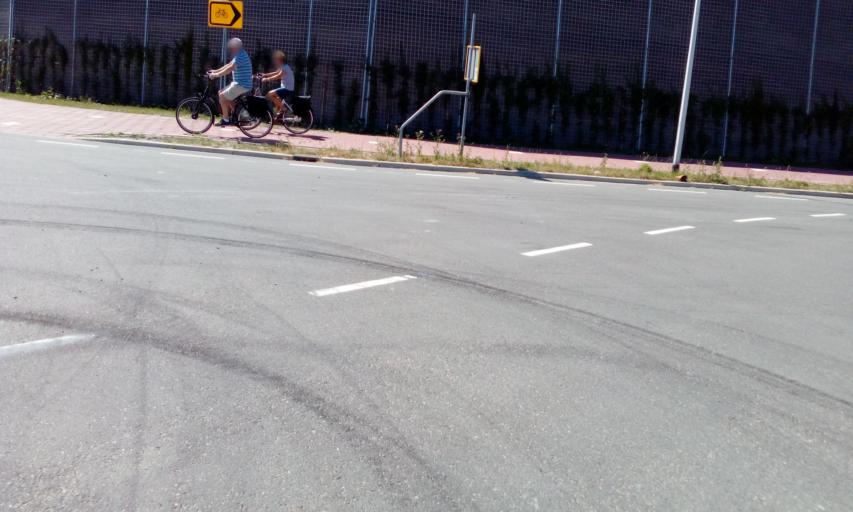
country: NL
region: South Holland
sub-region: Gemeente Westland
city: Honselersdijk
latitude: 51.9920
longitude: 4.2331
